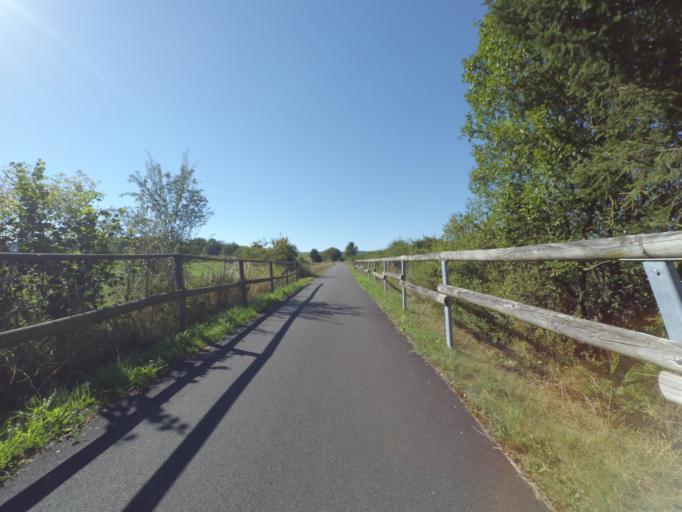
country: DE
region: Rheinland-Pfalz
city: Udler
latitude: 50.1392
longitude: 6.8848
